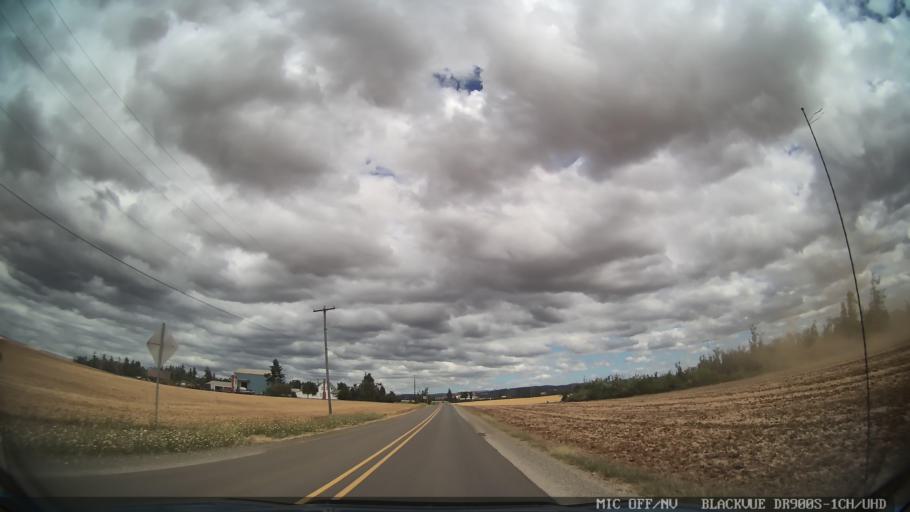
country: US
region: Oregon
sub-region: Marion County
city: Sublimity
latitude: 44.8663
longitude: -122.7894
